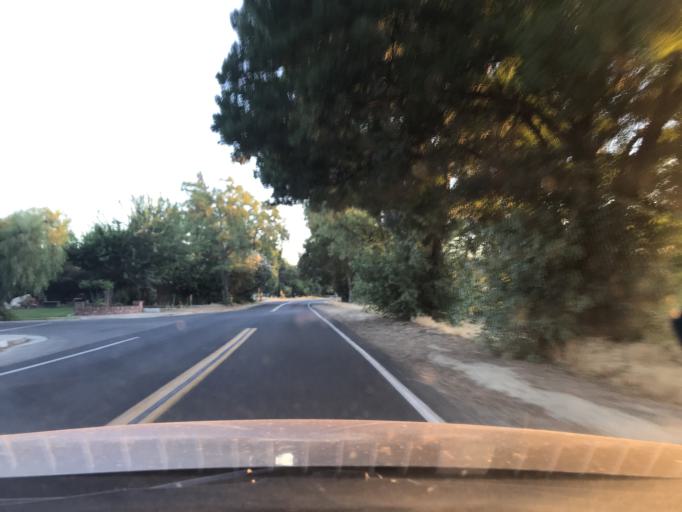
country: US
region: California
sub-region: Merced County
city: Merced
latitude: 37.3121
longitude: -120.4989
